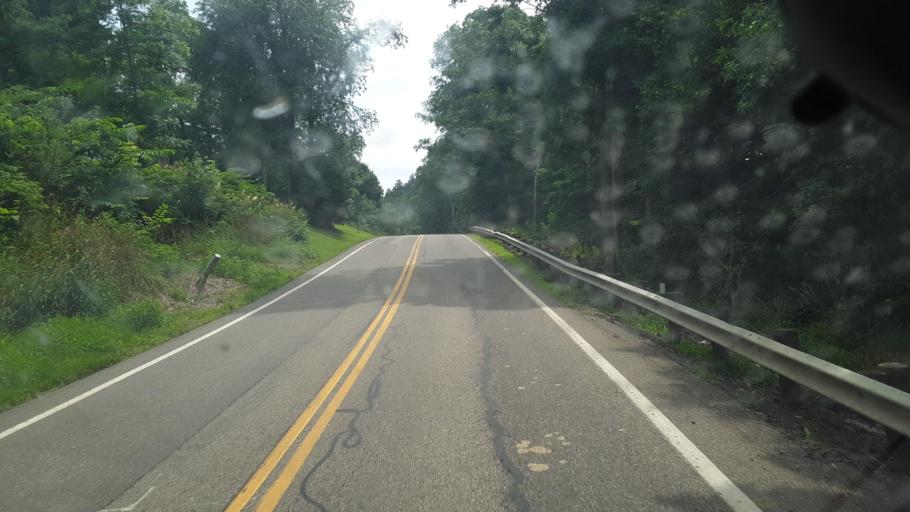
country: US
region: Ohio
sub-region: Coshocton County
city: West Lafayette
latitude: 40.3735
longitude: -81.7248
